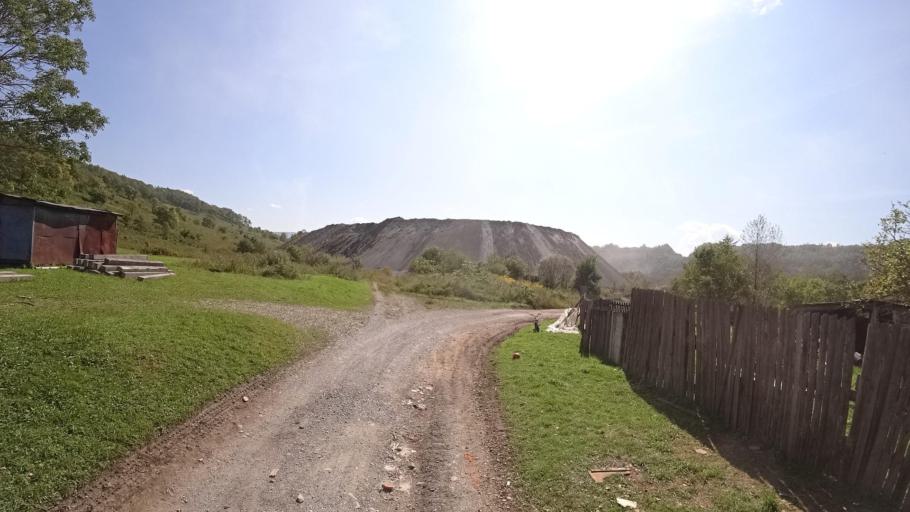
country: RU
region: Jewish Autonomous Oblast
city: Londoko
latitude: 49.0217
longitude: 131.9338
